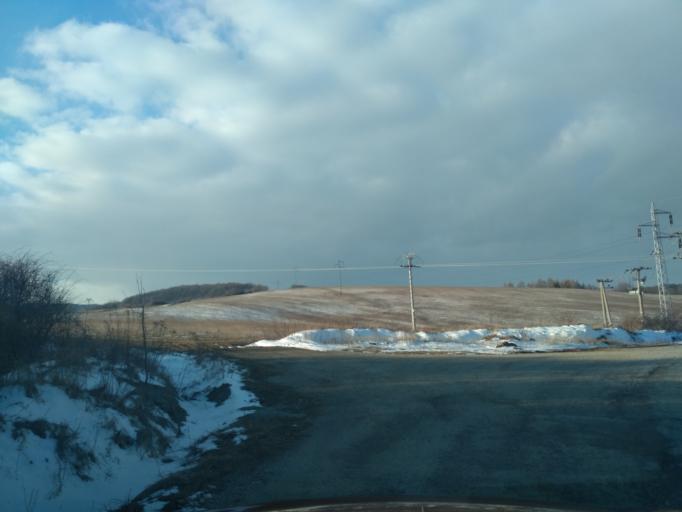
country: SK
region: Kosicky
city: Kosice
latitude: 48.7333
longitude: 21.1465
